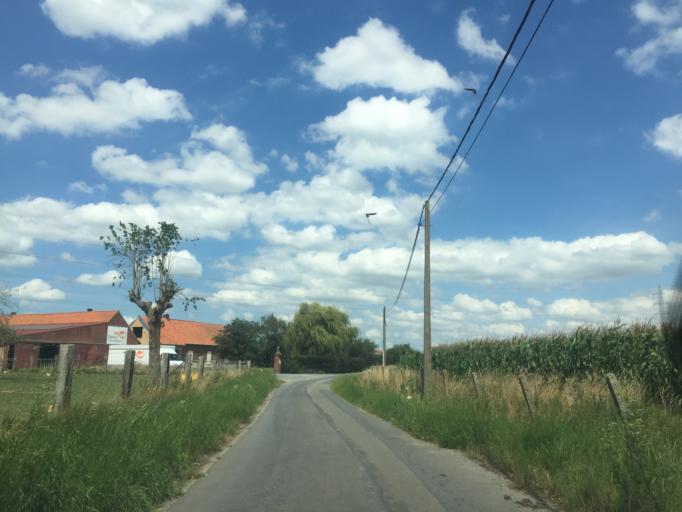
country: BE
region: Flanders
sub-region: Provincie West-Vlaanderen
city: Staden
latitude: 50.9529
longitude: 2.9929
